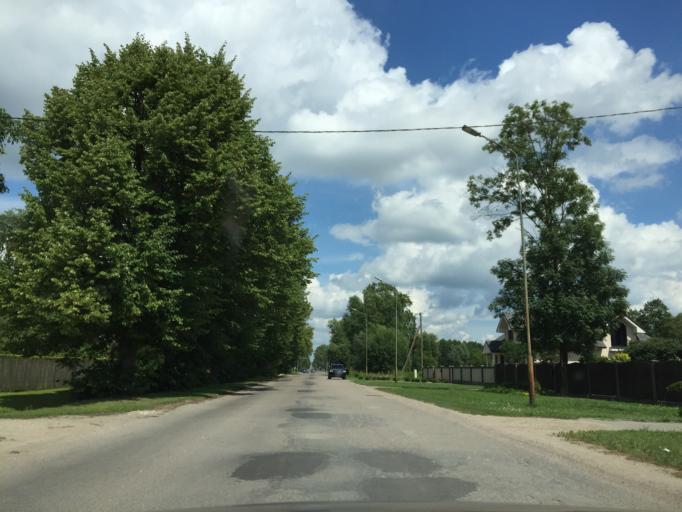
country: LV
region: Jelgava
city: Jelgava
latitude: 56.6405
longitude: 23.6935
